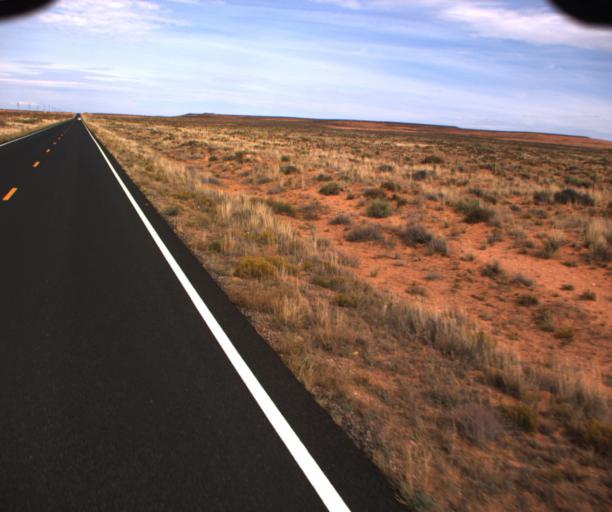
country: US
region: Arizona
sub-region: Apache County
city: Many Farms
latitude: 36.8423
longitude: -109.6410
